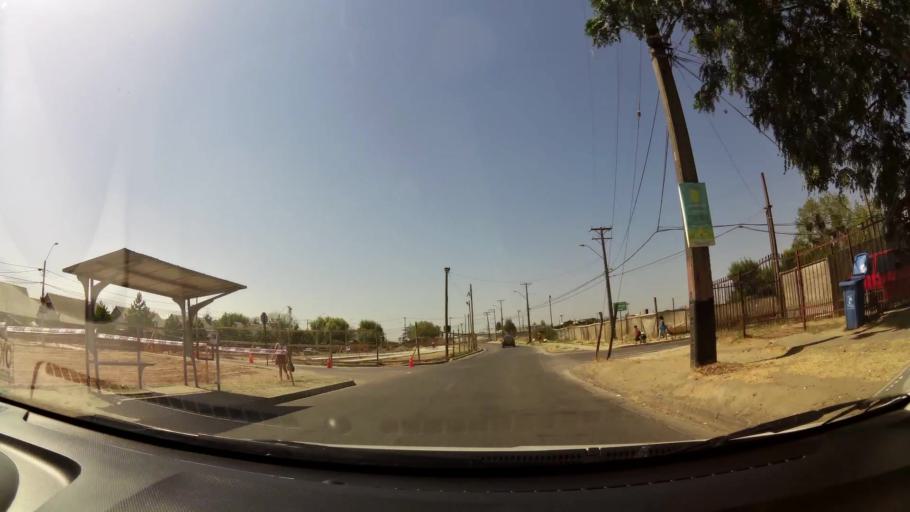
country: CL
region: Maule
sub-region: Provincia de Talca
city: Talca
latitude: -35.4176
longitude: -71.6366
